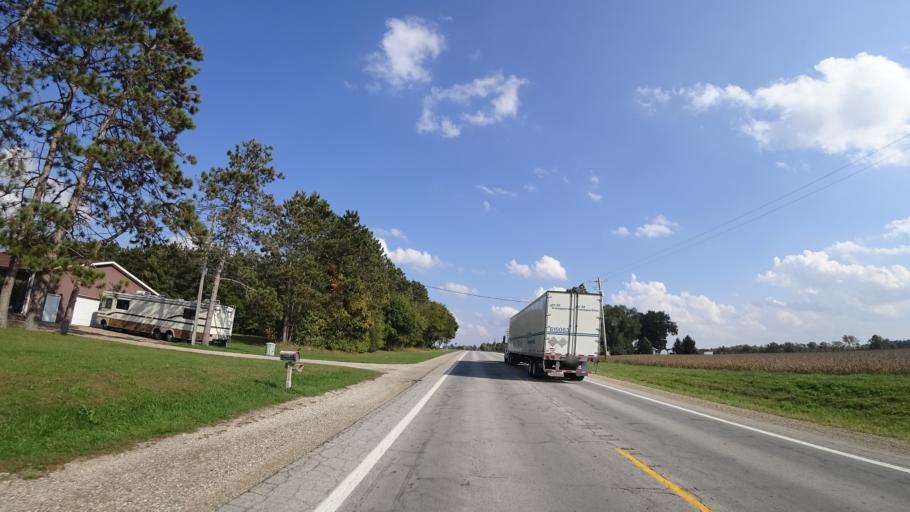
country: US
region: Michigan
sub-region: Saint Joseph County
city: Colon
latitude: 42.0102
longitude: -85.3830
